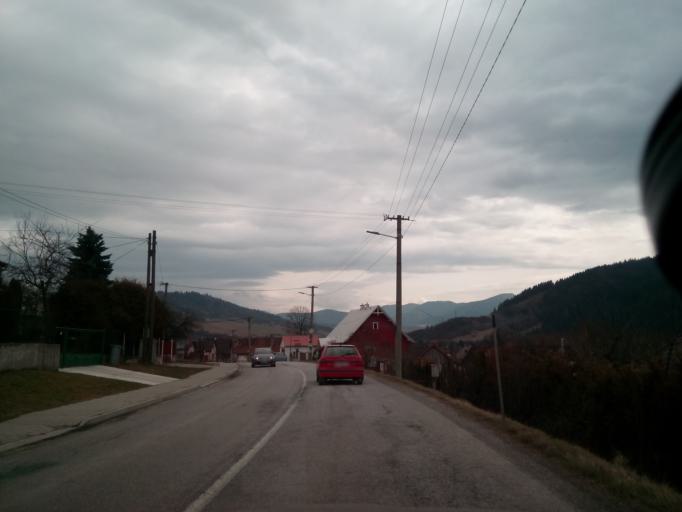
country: SK
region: Zilinsky
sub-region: Okres Dolny Kubin
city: Dolny Kubin
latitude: 49.1955
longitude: 19.1909
